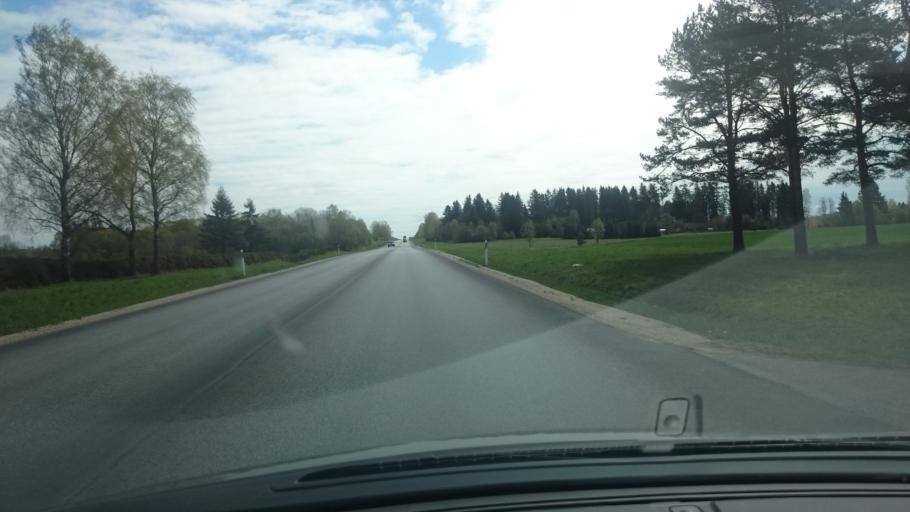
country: EE
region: Laeaene-Virumaa
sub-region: Haljala vald
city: Haljala
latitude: 59.4358
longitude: 26.1630
